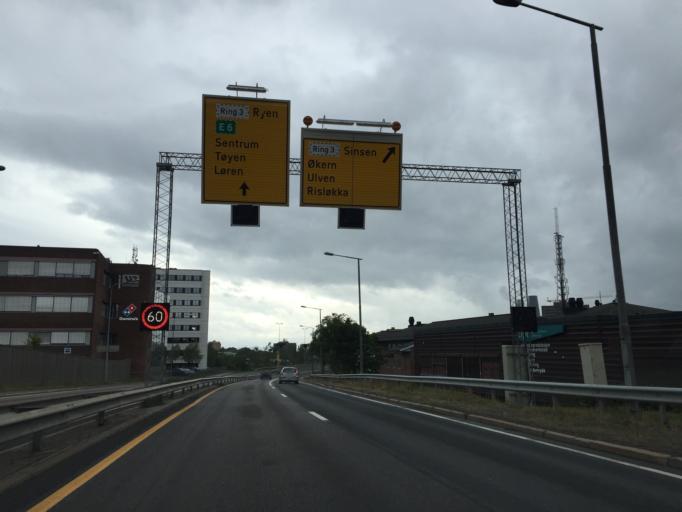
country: NO
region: Oslo
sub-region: Oslo
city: Oslo
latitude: 59.9285
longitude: 10.8161
